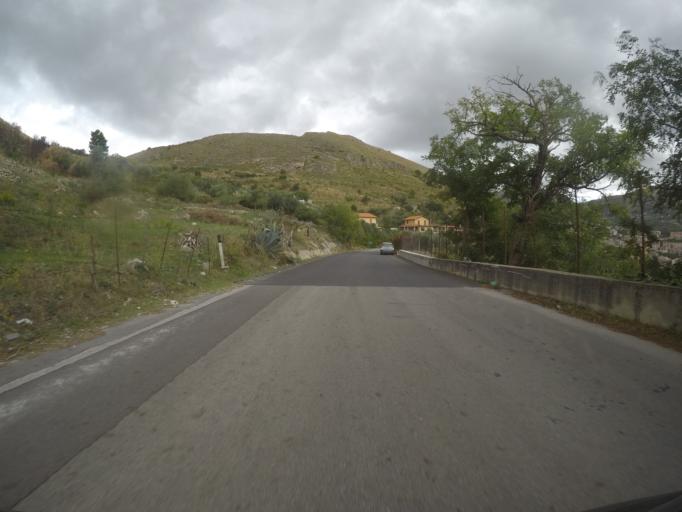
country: IT
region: Sicily
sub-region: Palermo
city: Montelepre
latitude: 38.0952
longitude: 13.1702
